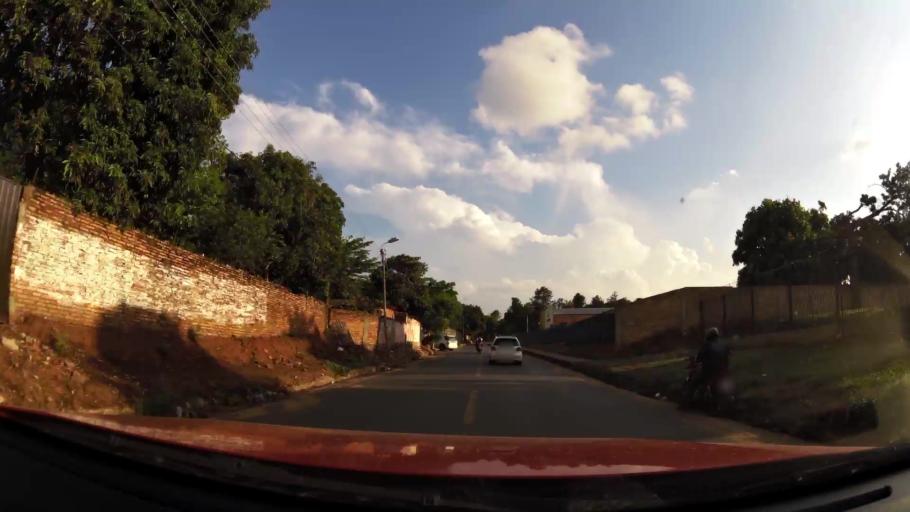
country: PY
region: Central
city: Fernando de la Mora
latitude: -25.3488
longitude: -57.5198
